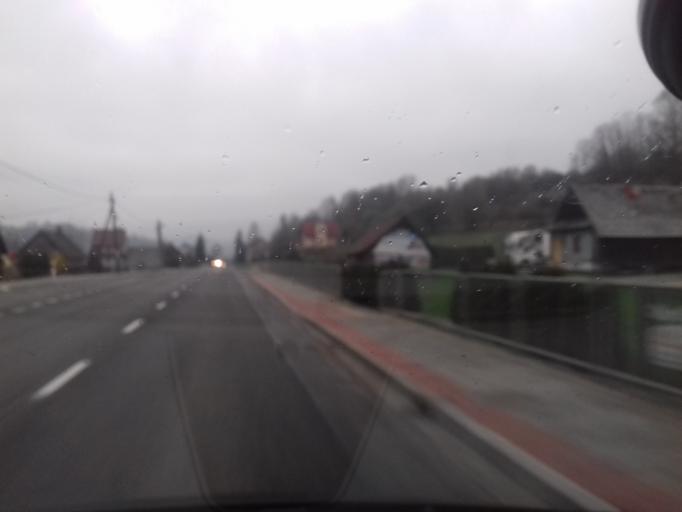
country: PL
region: Lesser Poland Voivodeship
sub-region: Powiat limanowski
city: Mszana Gorna
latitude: 49.6861
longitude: 20.1091
